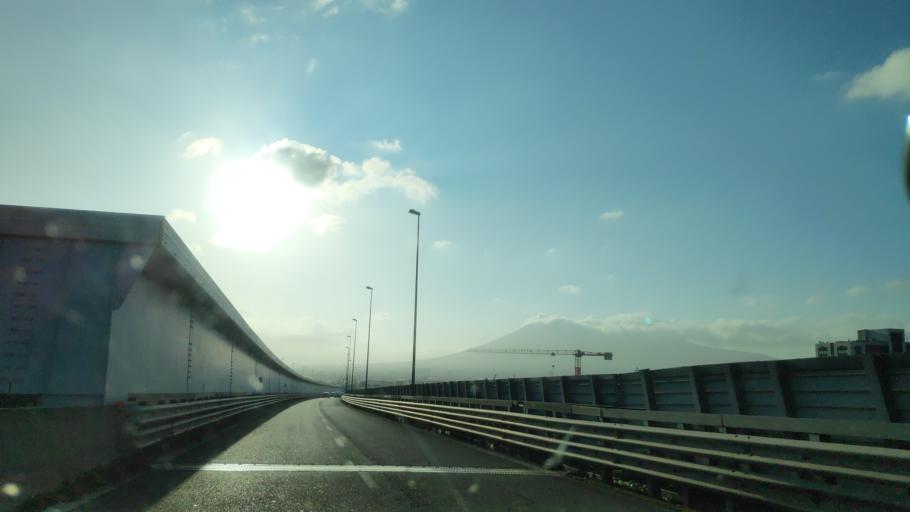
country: IT
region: Campania
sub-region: Provincia di Napoli
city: Napoli
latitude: 40.8632
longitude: 14.2797
